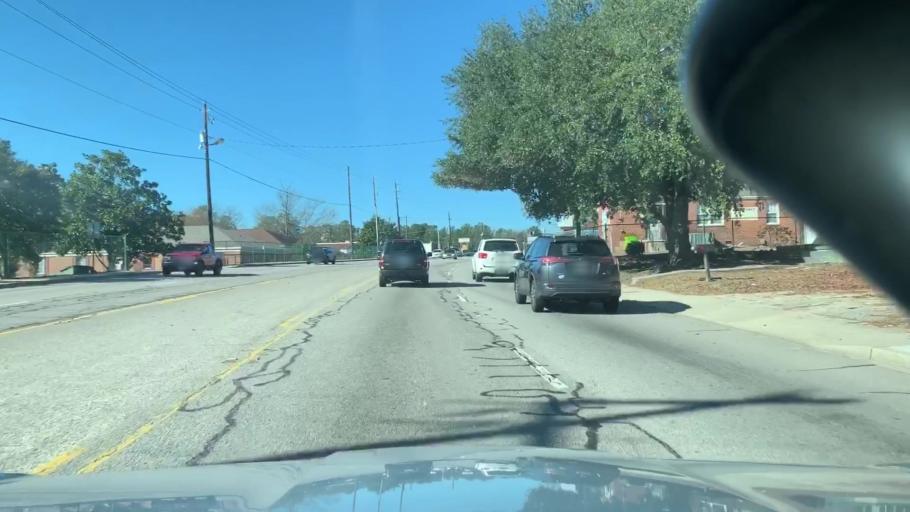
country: US
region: South Carolina
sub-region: Richland County
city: Woodfield
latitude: 34.0430
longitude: -80.9398
